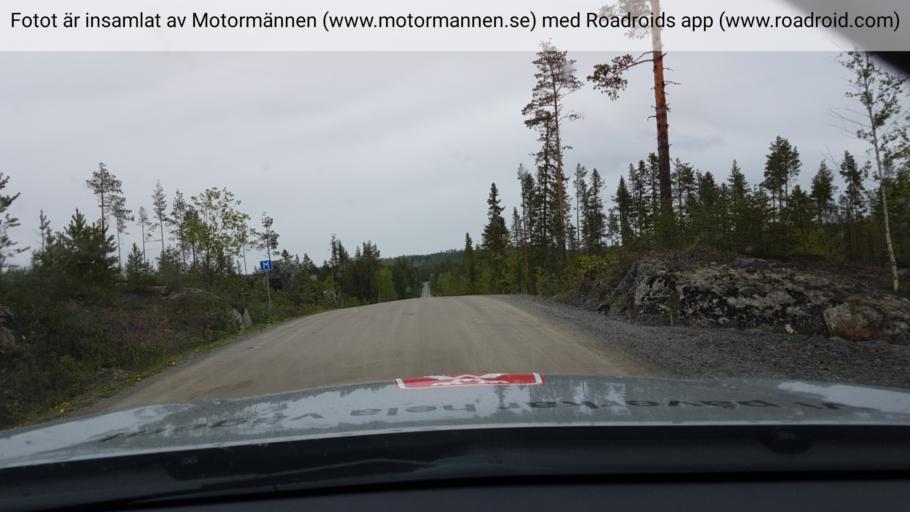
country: SE
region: Jaemtland
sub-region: Bergs Kommun
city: Hoverberg
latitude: 62.9262
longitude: 14.6442
